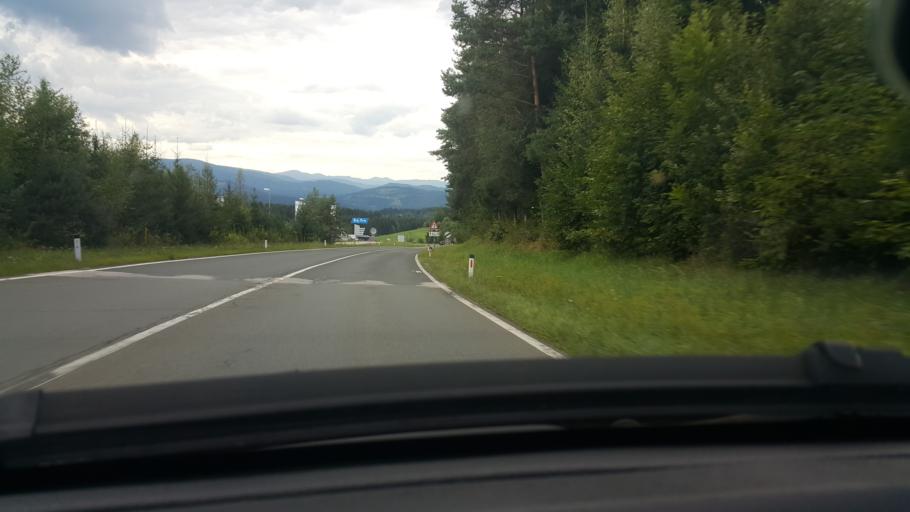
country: AT
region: Carinthia
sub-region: Politischer Bezirk Feldkirchen
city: Feldkirchen in Karnten
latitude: 46.6954
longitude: 14.1239
